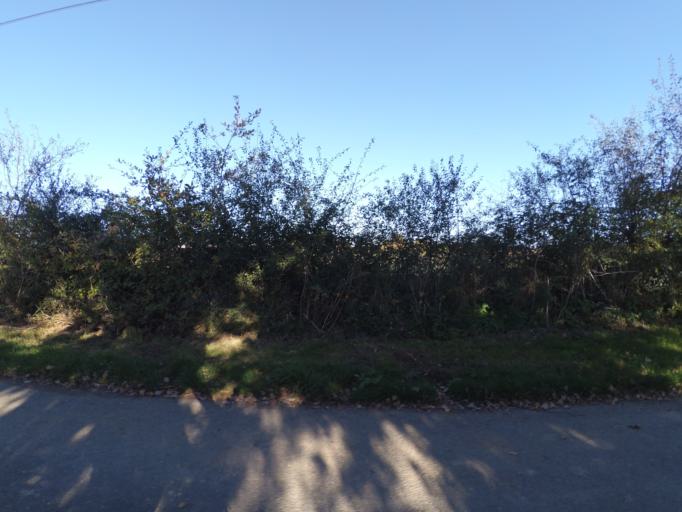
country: FR
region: Pays de la Loire
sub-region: Departement de la Vendee
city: Saint-Hilaire-de-Loulay
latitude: 46.9979
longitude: -1.3751
